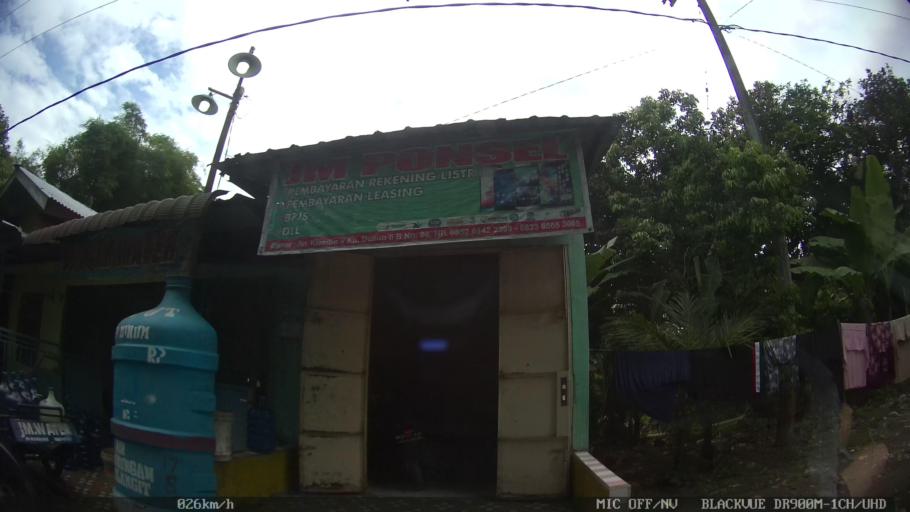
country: ID
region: North Sumatra
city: Sunggal
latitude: 3.6466
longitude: 98.5929
